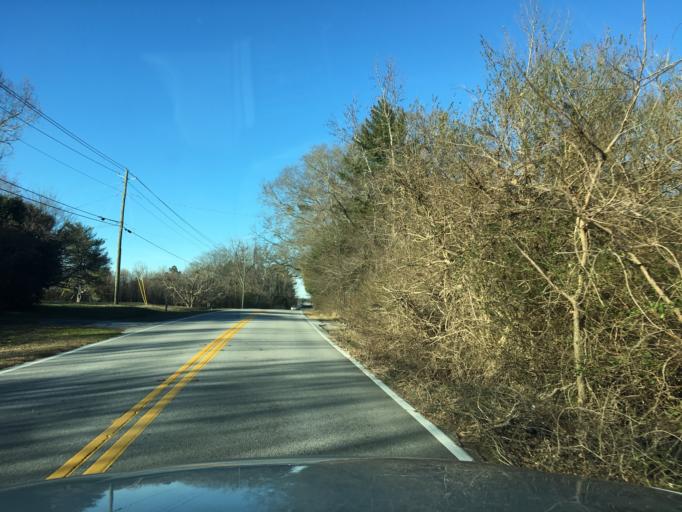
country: US
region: Georgia
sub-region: Rockdale County
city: Conyers
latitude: 33.6788
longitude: -84.0298
